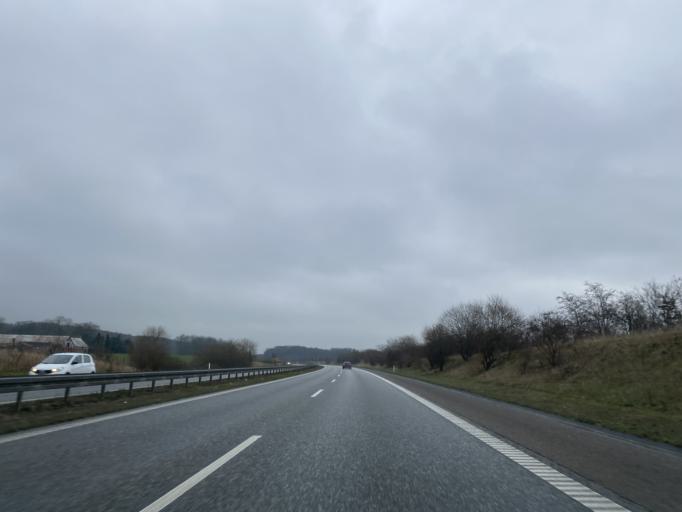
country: DK
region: Central Jutland
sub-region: Skanderborg Kommune
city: Skovby
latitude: 56.1420
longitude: 9.9502
